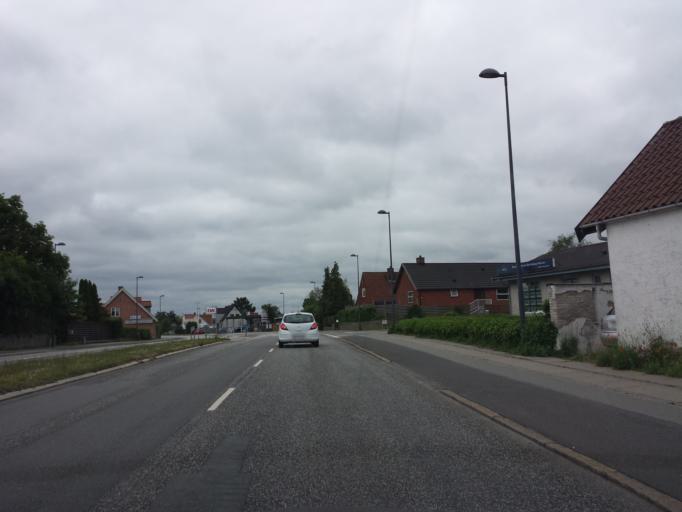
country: DK
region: Capital Region
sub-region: Ballerup Kommune
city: Ballerup
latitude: 55.7262
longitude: 12.3568
